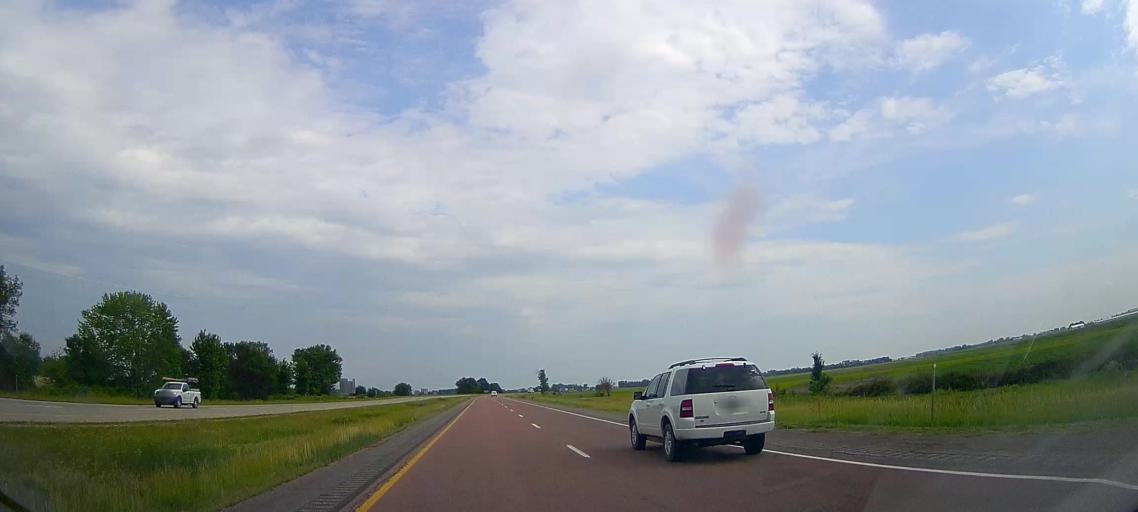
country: US
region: Iowa
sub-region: Monona County
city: Onawa
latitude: 42.0119
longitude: -96.1204
